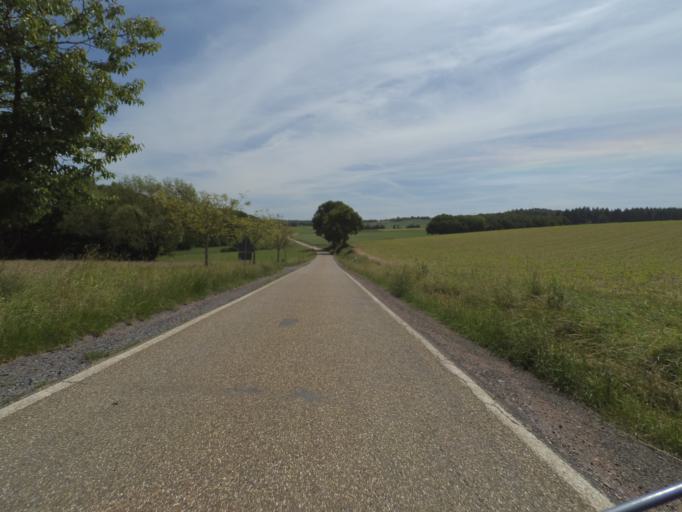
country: DE
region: Rheinland-Pfalz
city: Montenich
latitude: 50.2147
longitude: 7.3036
